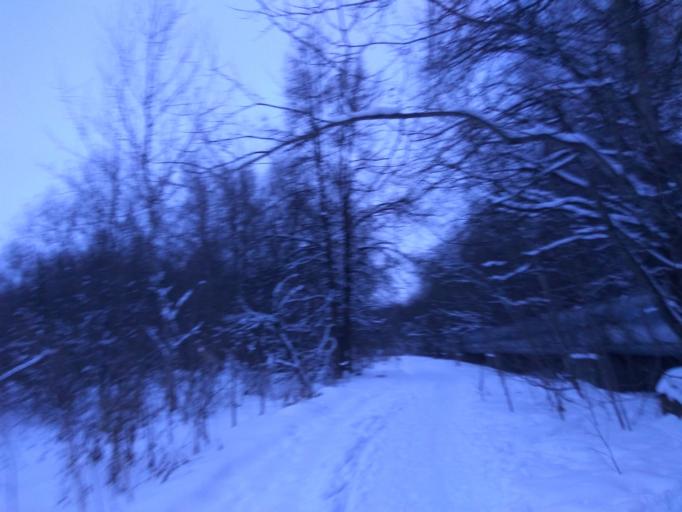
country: RU
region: Moscow
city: Biryulevo
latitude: 55.5900
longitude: 37.6993
